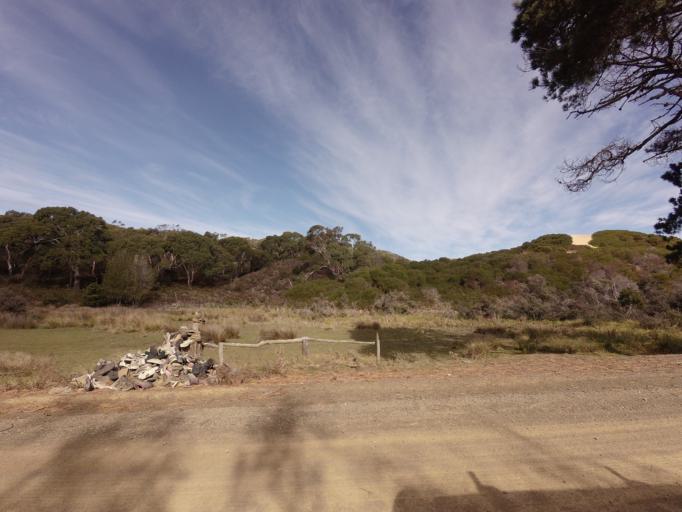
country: AU
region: Tasmania
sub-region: Clarence
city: Sandford
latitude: -43.0841
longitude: 147.6790
